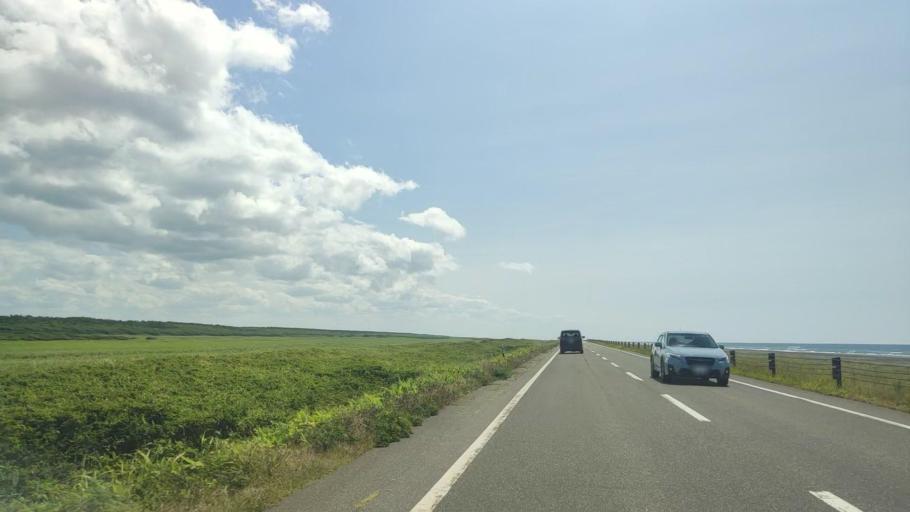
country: JP
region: Hokkaido
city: Wakkanai
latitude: 45.1729
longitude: 141.5807
